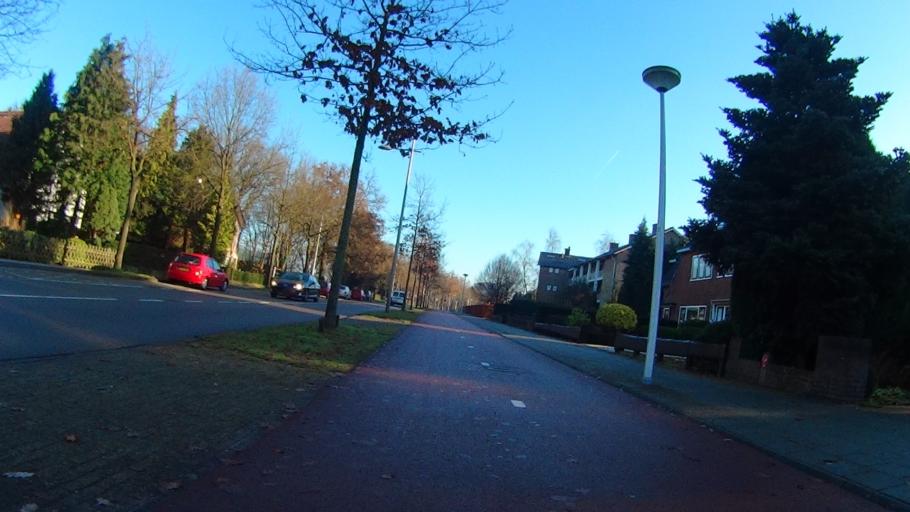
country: NL
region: Utrecht
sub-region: Gemeente Amersfoort
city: Amersfoort
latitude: 52.1524
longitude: 5.3625
